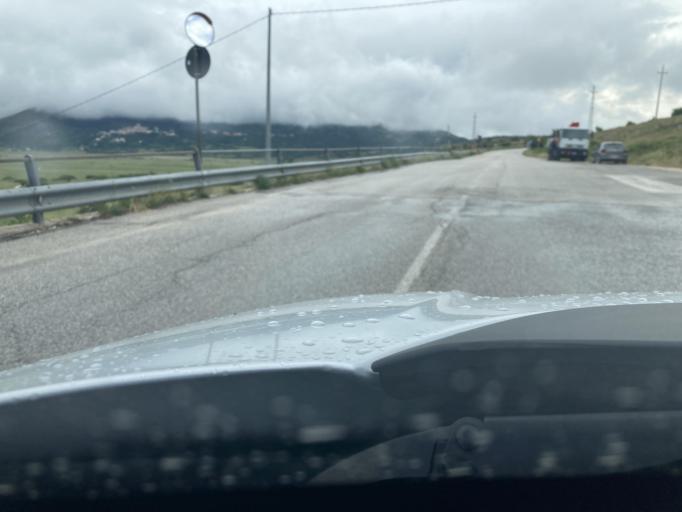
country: IT
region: Abruzzo
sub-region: Provincia dell' Aquila
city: Rocca di Mezzo
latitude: 42.2357
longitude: 13.5320
